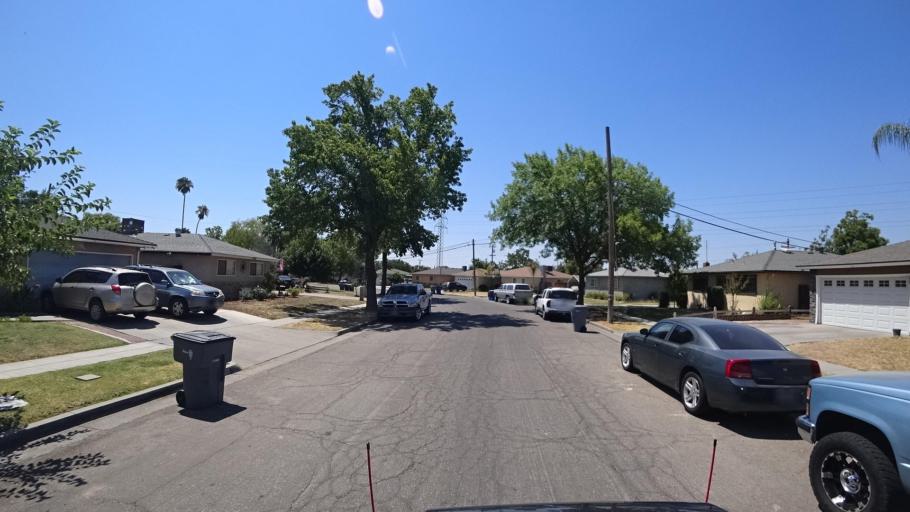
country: US
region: California
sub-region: Fresno County
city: Sunnyside
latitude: 36.7640
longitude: -119.7337
